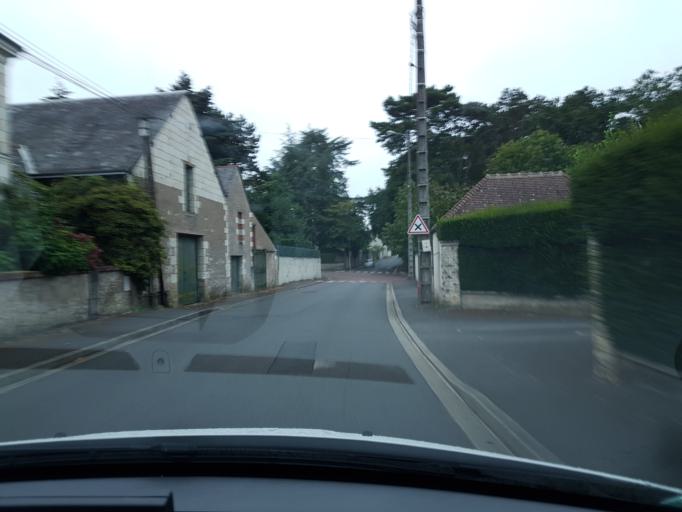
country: FR
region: Centre
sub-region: Departement d'Indre-et-Loire
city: Saint-Avertin
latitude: 47.3670
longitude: 0.7391
